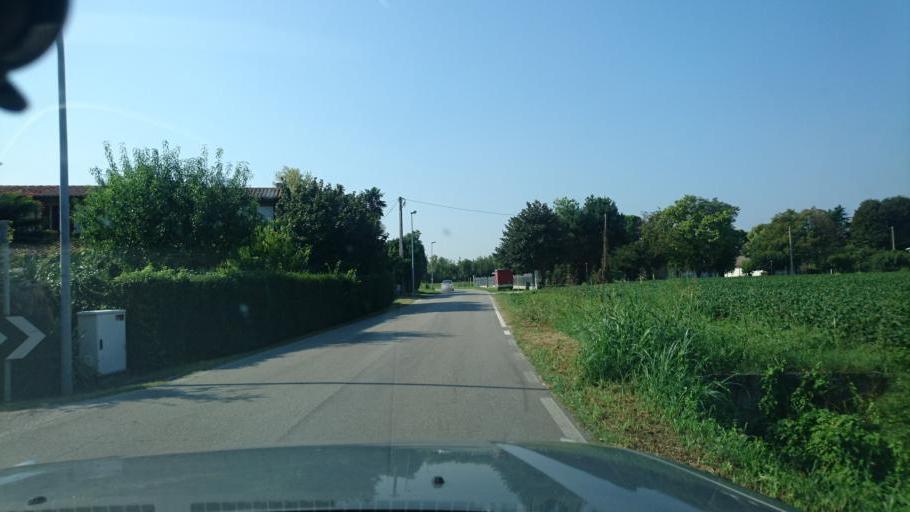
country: IT
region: Veneto
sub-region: Provincia di Padova
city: Casalserugo
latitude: 45.3070
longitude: 11.9067
